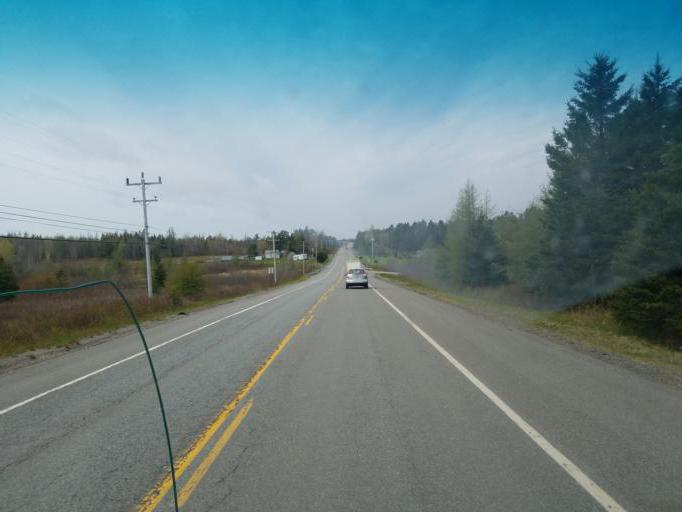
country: US
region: Maine
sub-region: Washington County
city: East Machias
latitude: 44.7611
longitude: -67.2174
